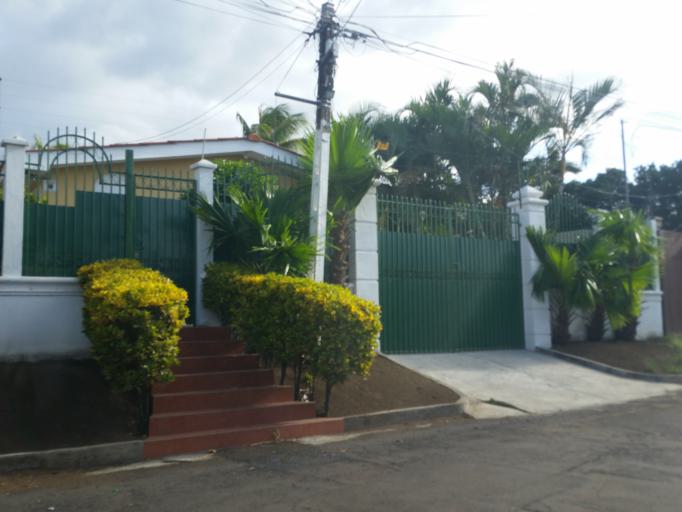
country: NI
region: Managua
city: Managua
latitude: 12.0885
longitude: -86.2467
